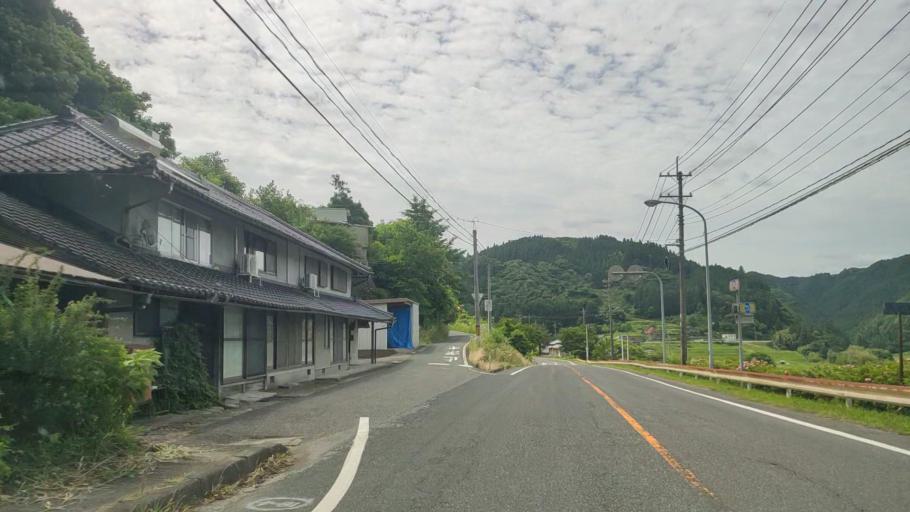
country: JP
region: Okayama
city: Niimi
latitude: 35.0963
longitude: 133.6529
